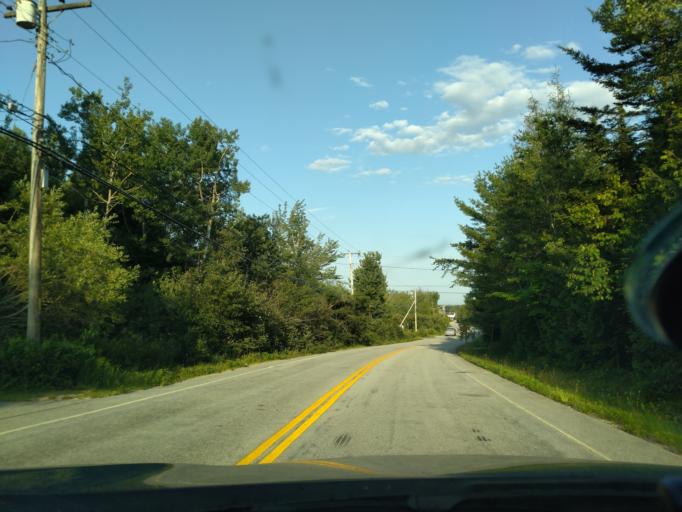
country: US
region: Maine
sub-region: Hancock County
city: Gouldsboro
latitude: 44.3916
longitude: -68.0499
